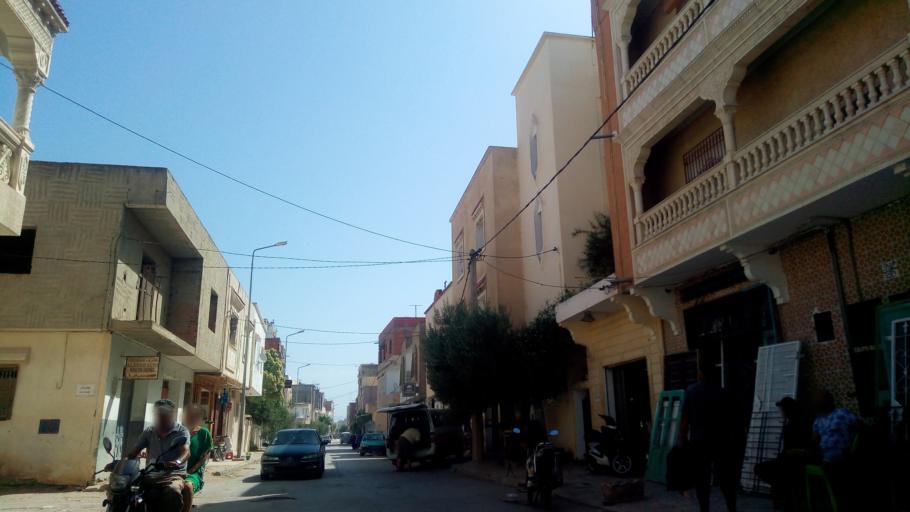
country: TN
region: Nabul
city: Dar Chabanne
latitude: 36.4682
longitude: 10.7418
